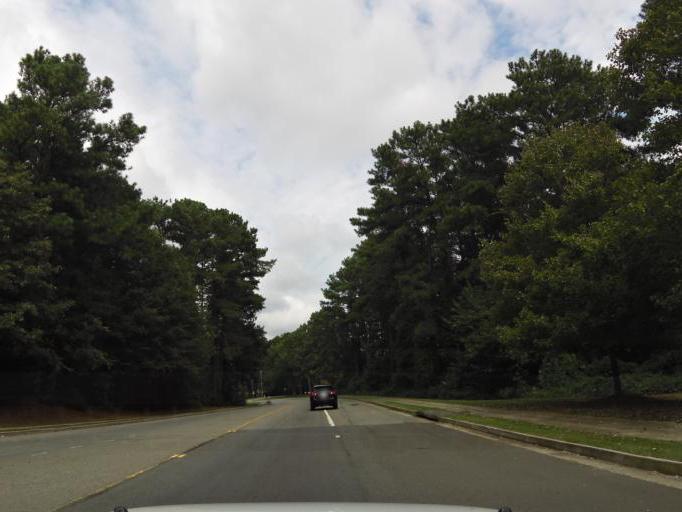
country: US
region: Georgia
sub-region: Cobb County
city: Kennesaw
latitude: 34.0041
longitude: -84.6219
